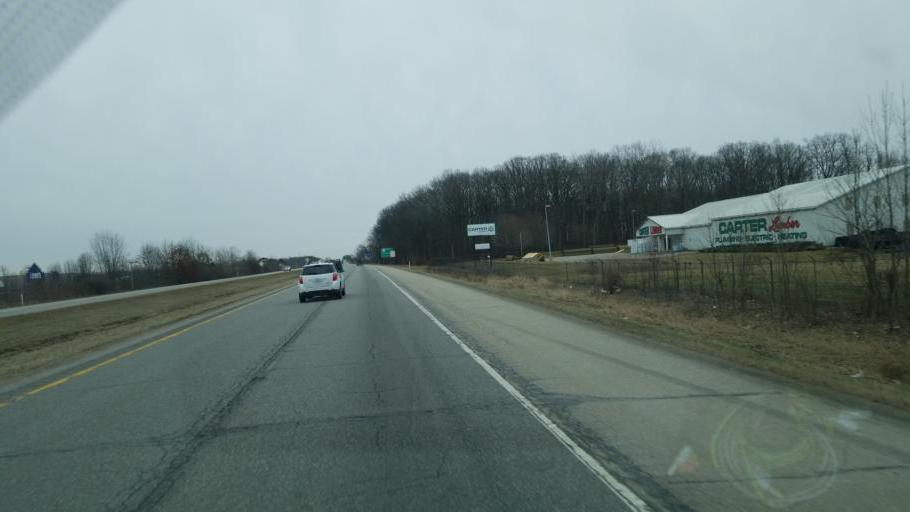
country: US
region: Indiana
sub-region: Marshall County
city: Plymouth
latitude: 41.3614
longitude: -86.3263
